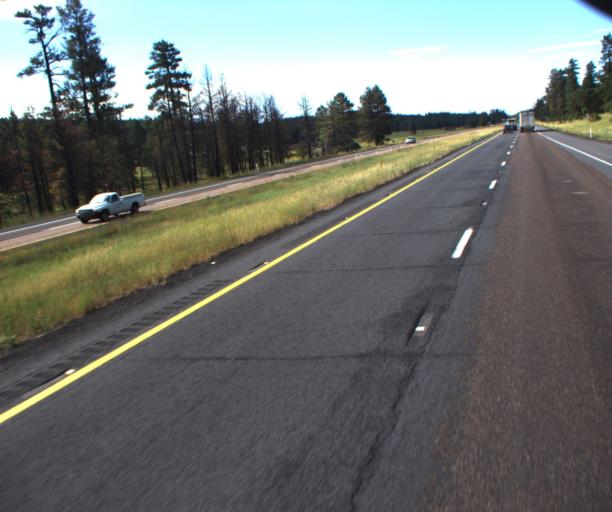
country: US
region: Arizona
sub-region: Coconino County
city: Mountainaire
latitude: 35.0134
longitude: -111.6851
